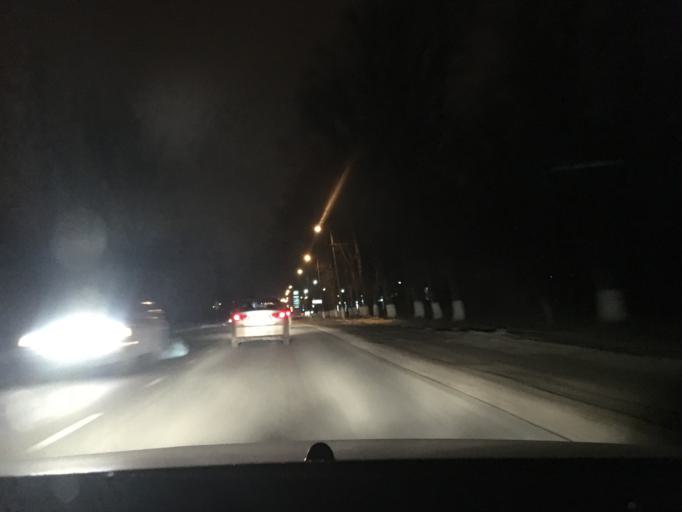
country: RU
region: Tula
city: Shchekino
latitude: 54.0225
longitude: 37.5191
